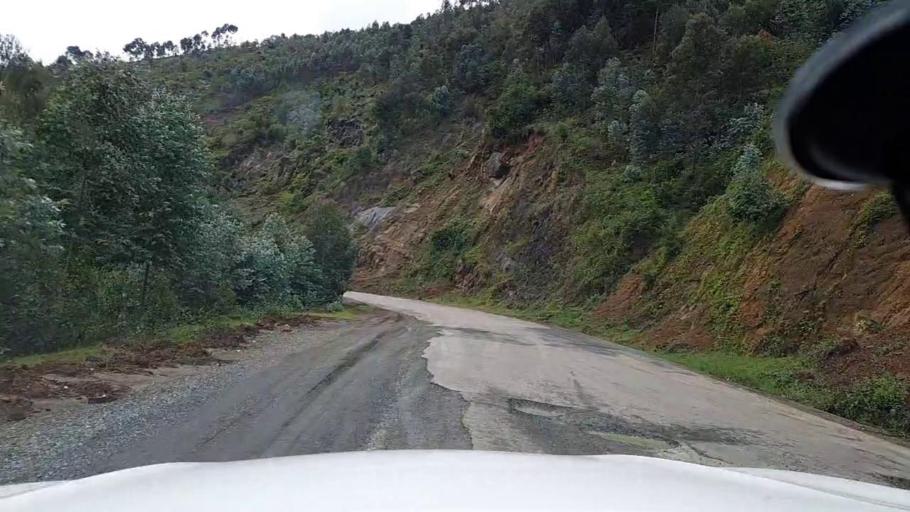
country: RW
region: Western Province
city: Kibuye
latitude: -2.0672
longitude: 29.5479
